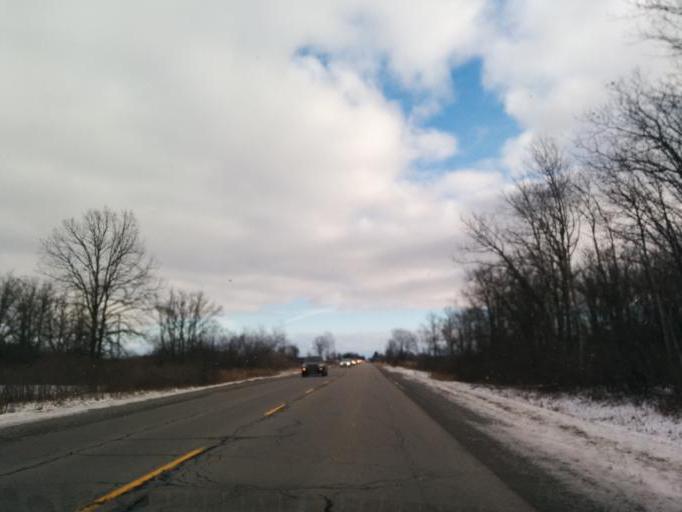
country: CA
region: Ontario
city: Brantford
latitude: 42.9844
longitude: -80.1126
